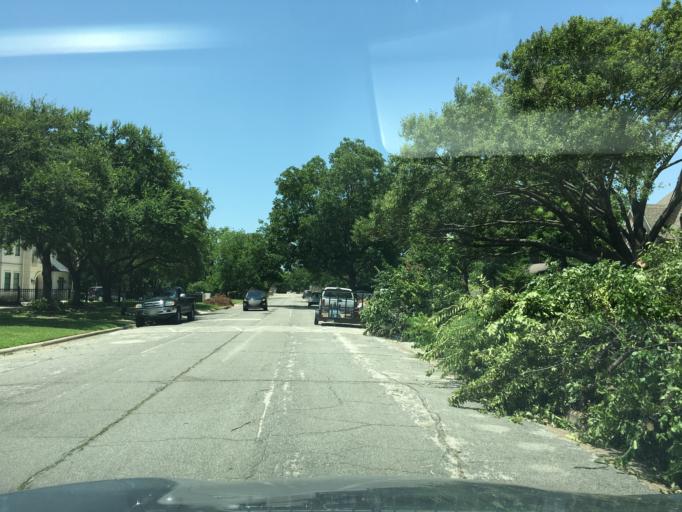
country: US
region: Texas
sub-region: Dallas County
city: University Park
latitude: 32.8866
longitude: -96.8060
